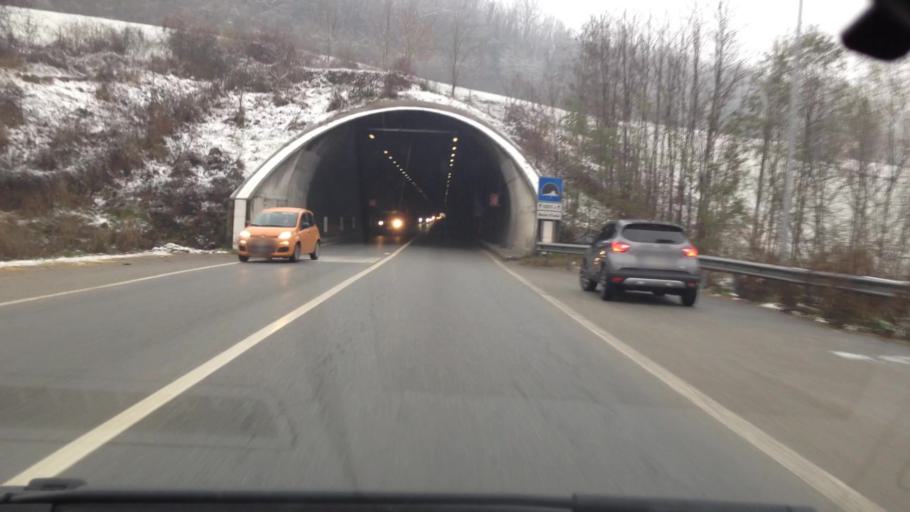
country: IT
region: Piedmont
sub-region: Provincia di Asti
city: Isola d'Asti
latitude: 44.8418
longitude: 8.1930
